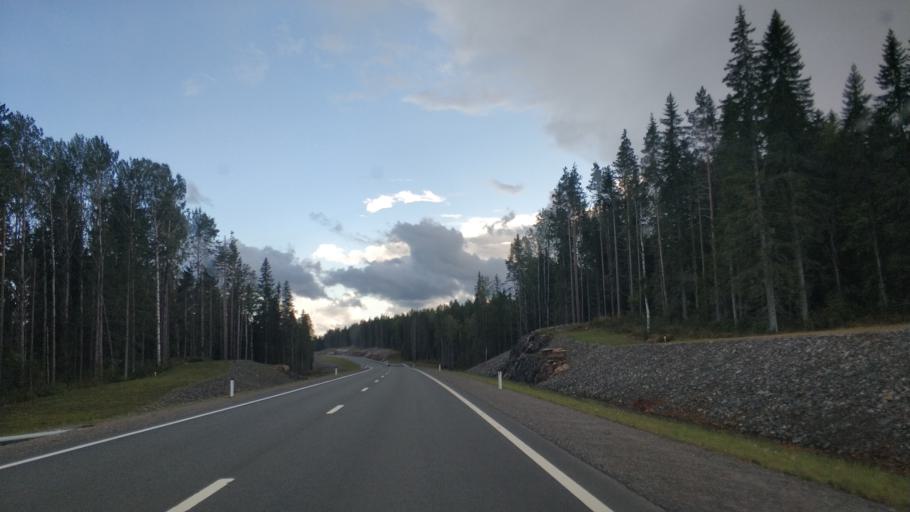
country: RU
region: Republic of Karelia
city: Lakhdenpokh'ya
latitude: 61.4193
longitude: 29.9632
